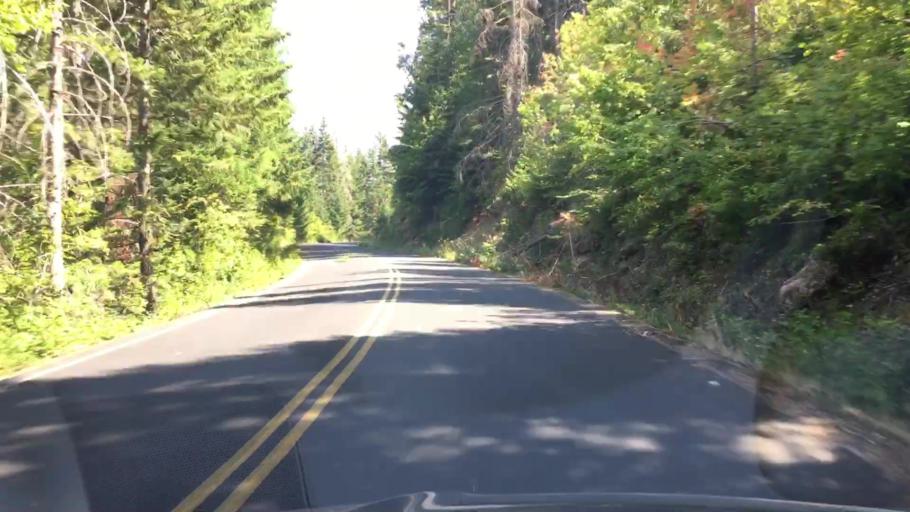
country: US
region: Washington
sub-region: Klickitat County
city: White Salmon
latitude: 46.0510
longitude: -121.5586
